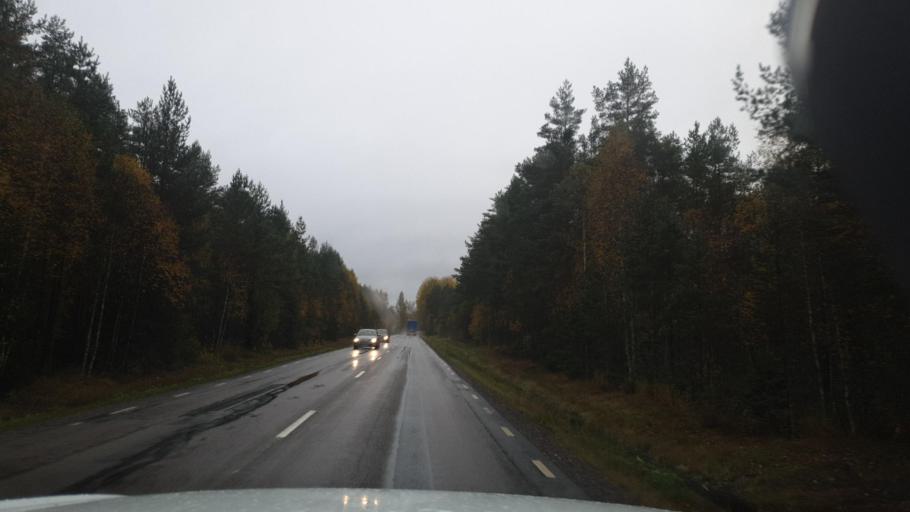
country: SE
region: Vaermland
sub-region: Eda Kommun
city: Charlottenberg
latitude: 59.8229
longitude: 12.2620
